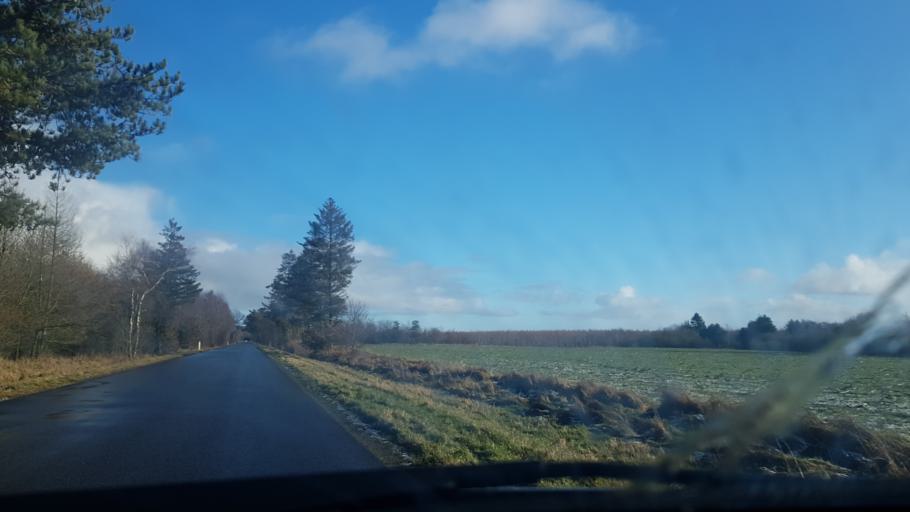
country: DK
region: South Denmark
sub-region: Haderslev Kommune
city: Vojens
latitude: 55.3184
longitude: 9.2094
